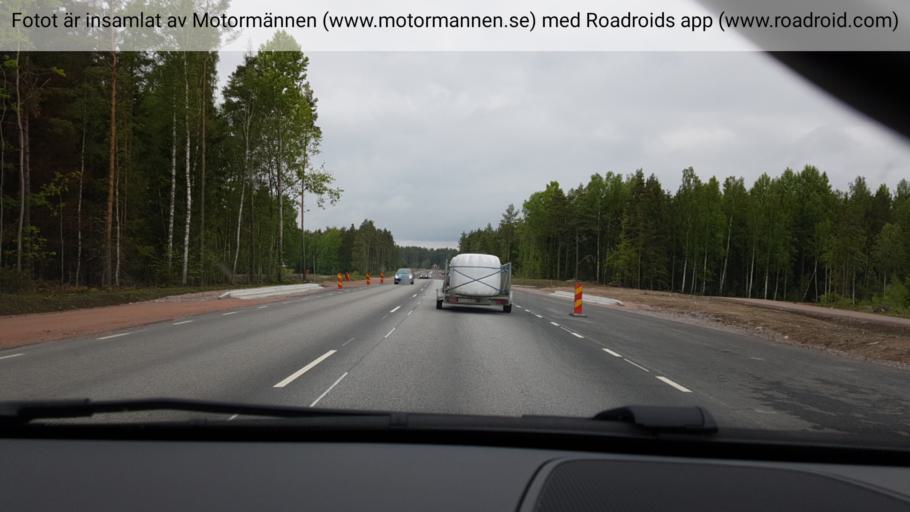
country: SE
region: Uppsala
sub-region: Osthammars Kommun
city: Gimo
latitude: 60.0991
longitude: 18.1256
